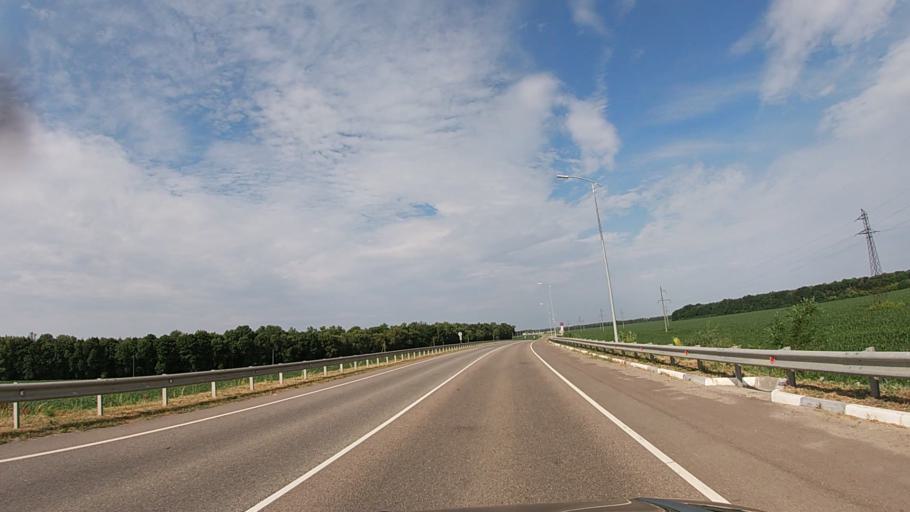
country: RU
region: Belgorod
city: Proletarskiy
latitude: 50.8026
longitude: 35.7361
